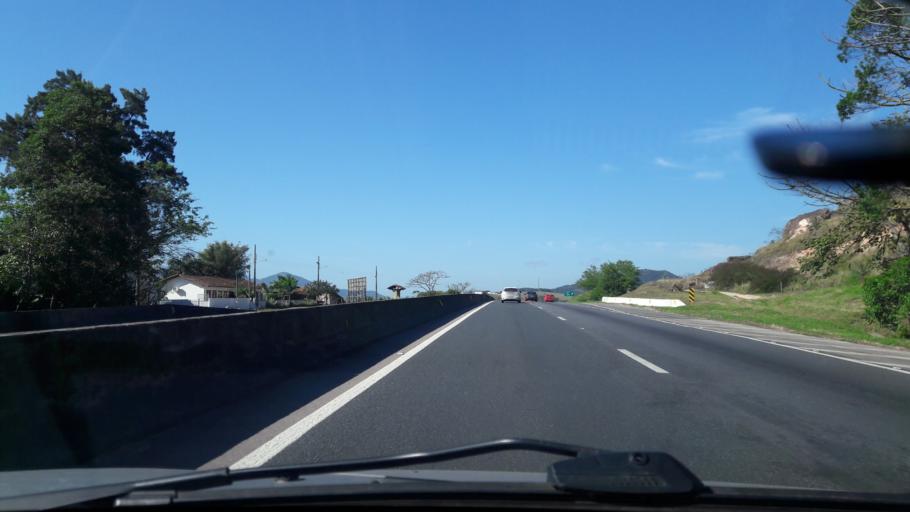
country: BR
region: Santa Catarina
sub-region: Tijucas
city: Tijucas
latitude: -27.2889
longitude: -48.6309
